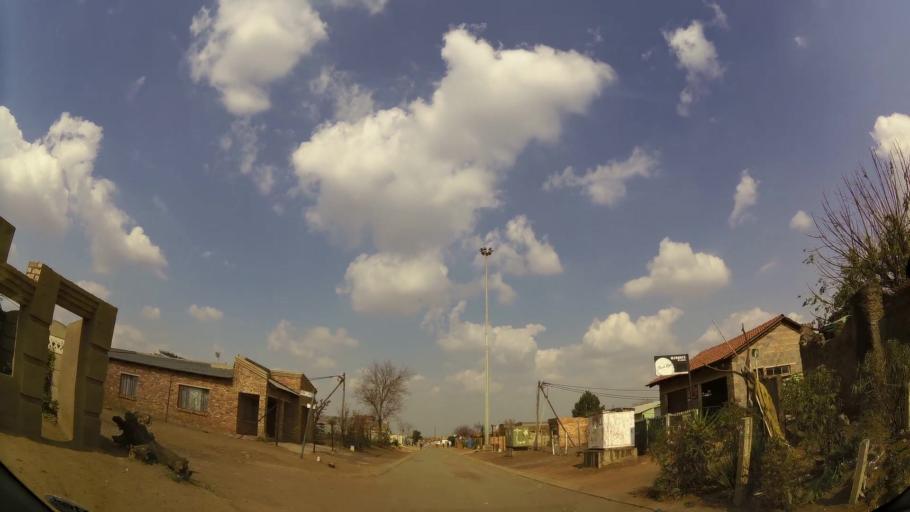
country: ZA
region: Gauteng
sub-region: Ekurhuleni Metropolitan Municipality
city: Springs
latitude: -26.1297
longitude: 28.4756
